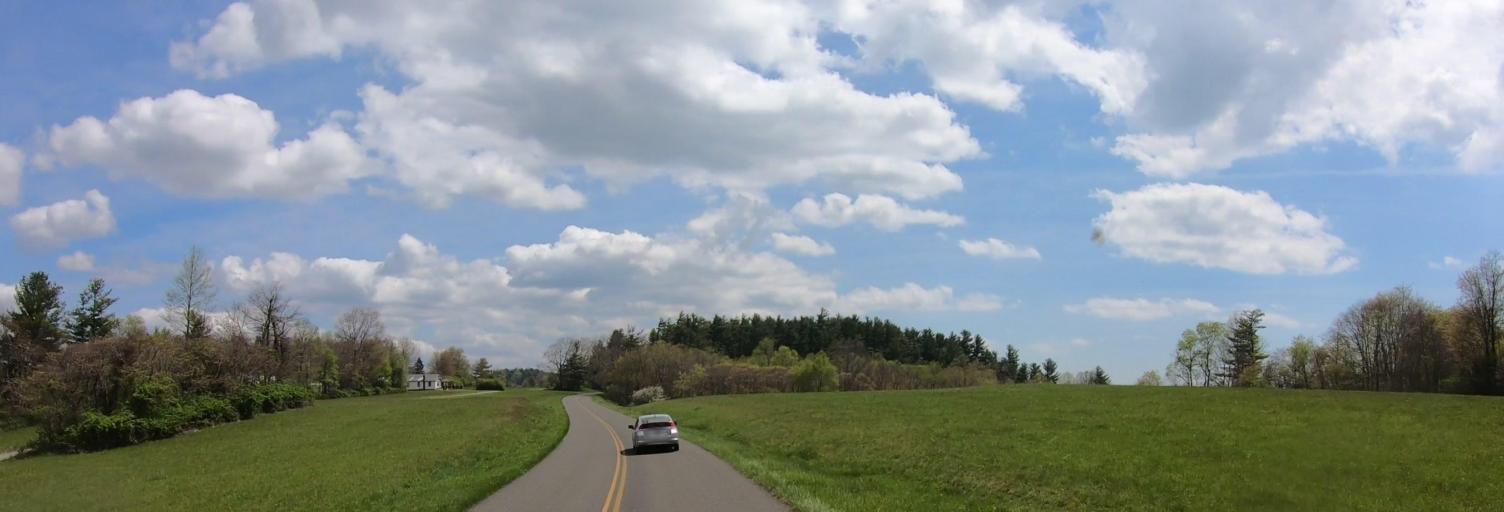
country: US
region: Virginia
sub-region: Carroll County
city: Cana
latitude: 36.6246
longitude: -80.7520
